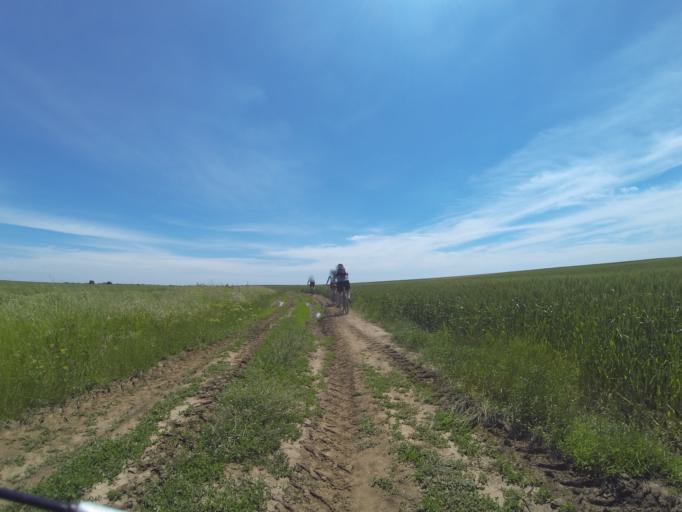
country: RO
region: Dolj
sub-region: Comuna Leu
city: Zanoaga
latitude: 44.1834
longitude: 24.0649
